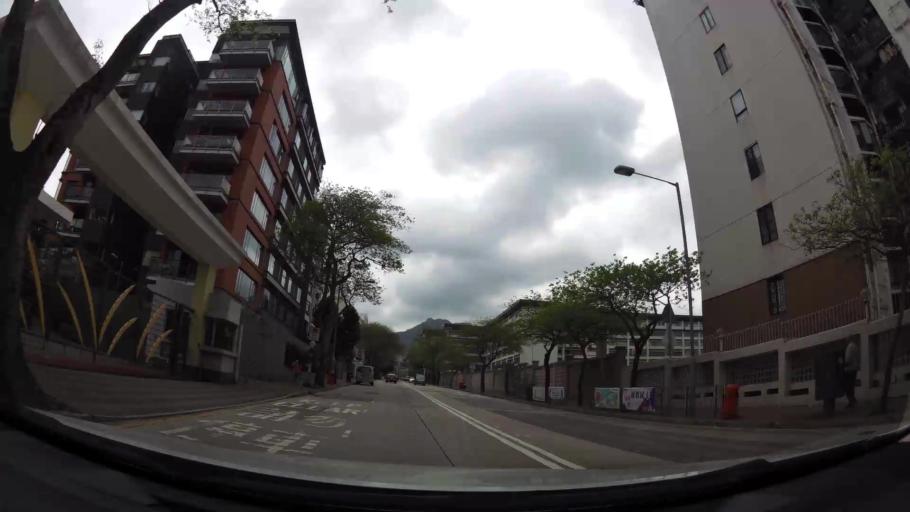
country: HK
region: Kowloon City
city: Kowloon
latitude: 22.3275
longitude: 114.1818
